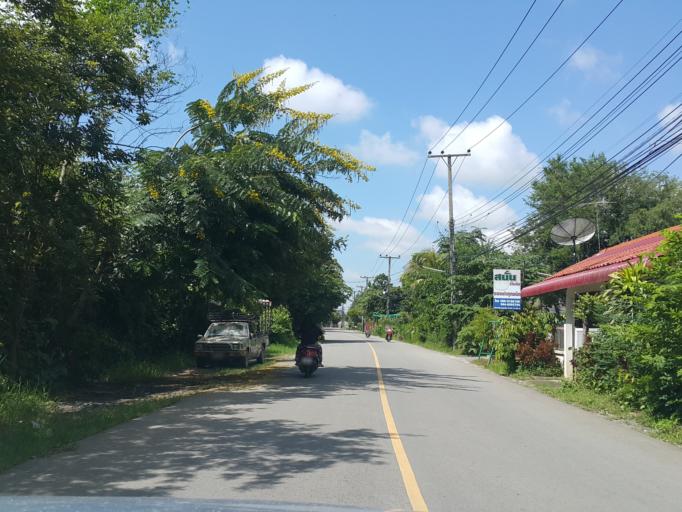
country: TH
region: Chiang Mai
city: San Kamphaeng
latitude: 18.7413
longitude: 99.1102
